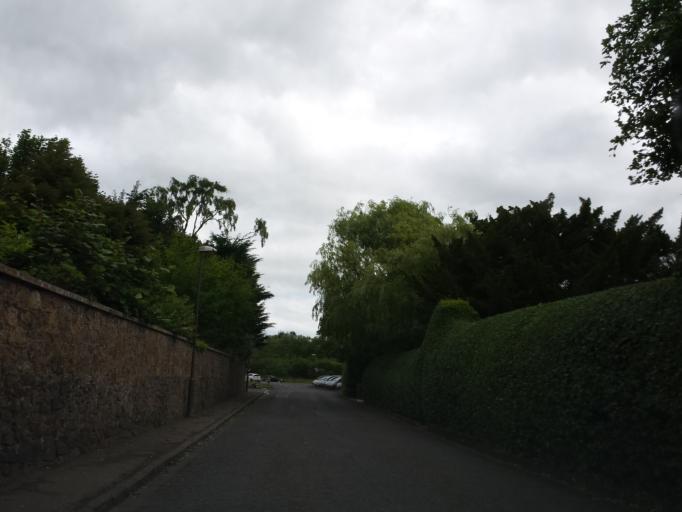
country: GB
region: Scotland
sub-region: East Lothian
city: Haddington
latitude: 55.9606
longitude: -2.7769
